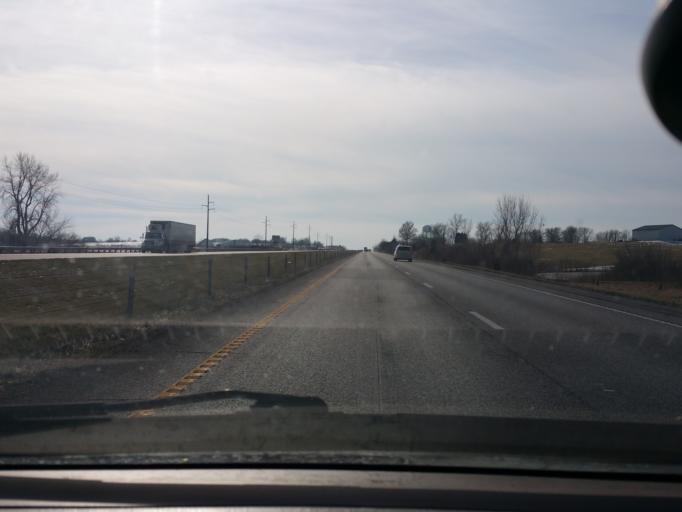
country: US
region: Missouri
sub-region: Clay County
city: Liberty
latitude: 39.3111
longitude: -94.4029
